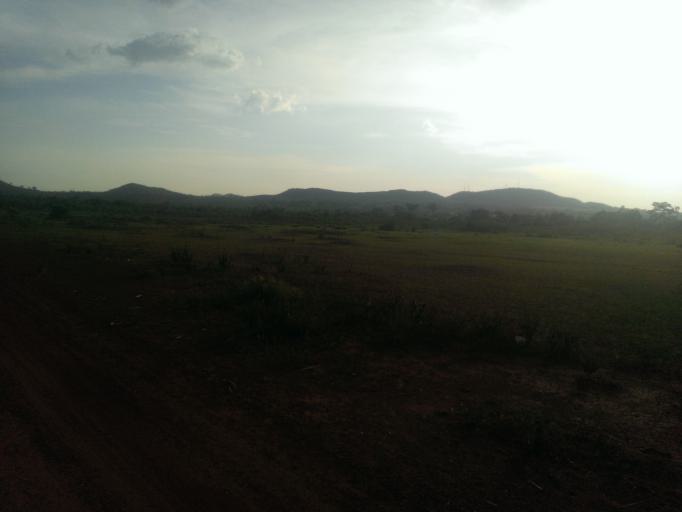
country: UG
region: Eastern Region
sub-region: Busia District
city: Busia
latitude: 0.5463
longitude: 33.9846
